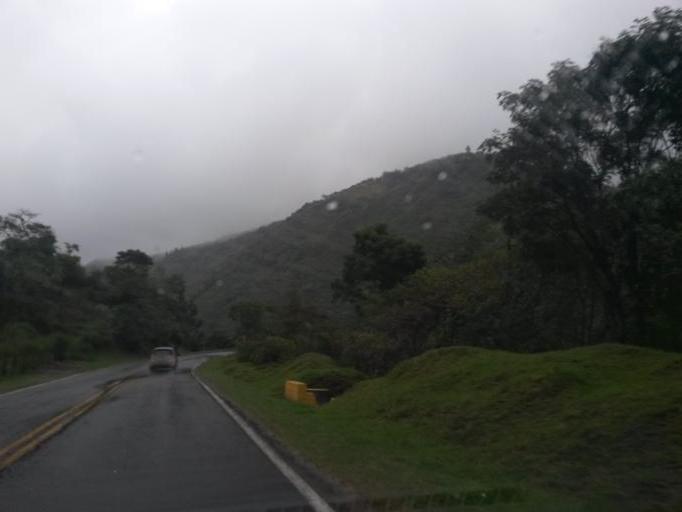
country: CO
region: Cauca
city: Popayan
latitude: 2.3797
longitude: -76.4962
